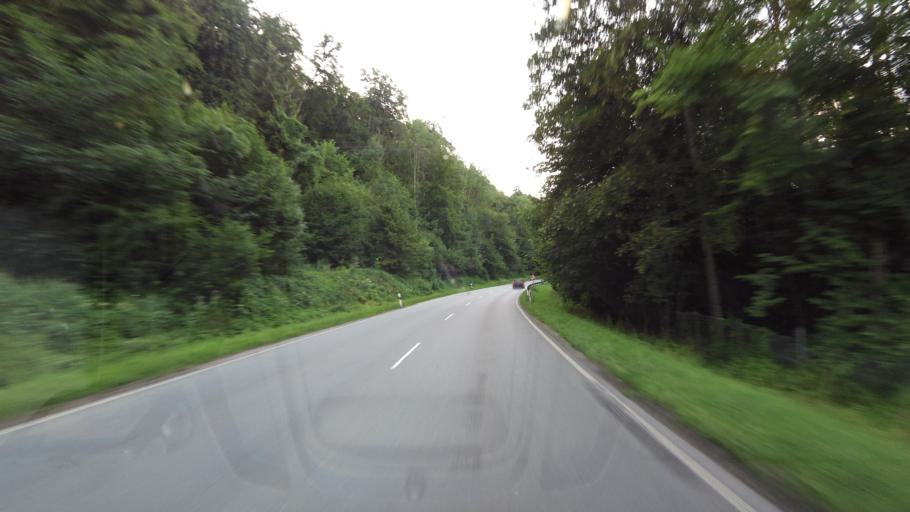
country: DE
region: Bavaria
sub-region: Upper Bavaria
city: Trostberg an der Alz
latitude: 48.0110
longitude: 12.5314
